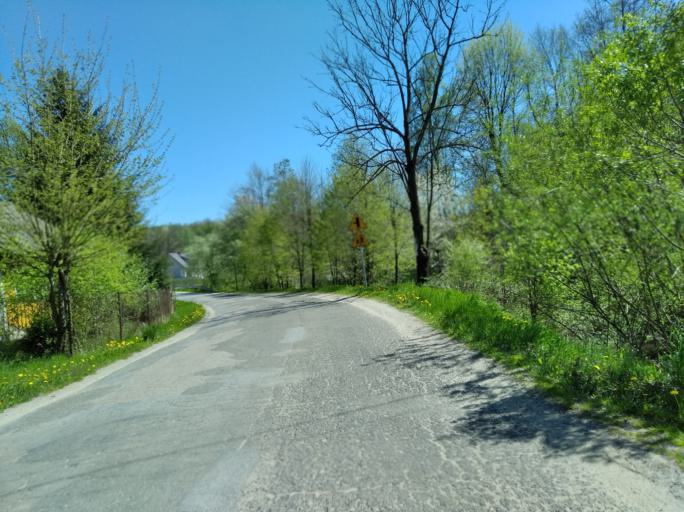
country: PL
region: Subcarpathian Voivodeship
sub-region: Powiat debicki
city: Brzostek
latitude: 49.9073
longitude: 21.4813
